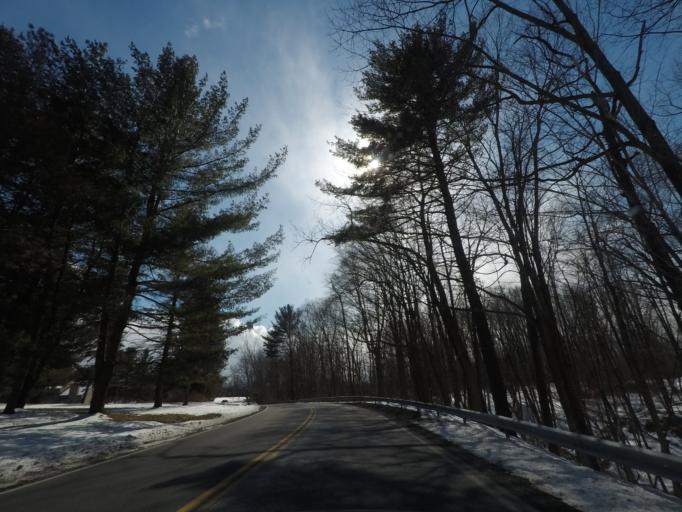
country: US
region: New York
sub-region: Albany County
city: McKownville
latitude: 42.6559
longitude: -73.8486
